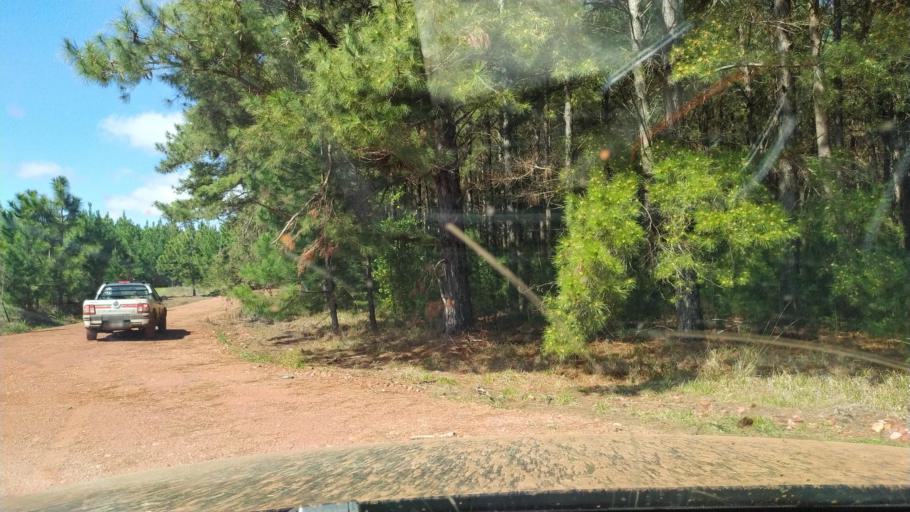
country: AR
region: Corrientes
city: Santo Tome
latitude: -28.4587
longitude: -55.9975
